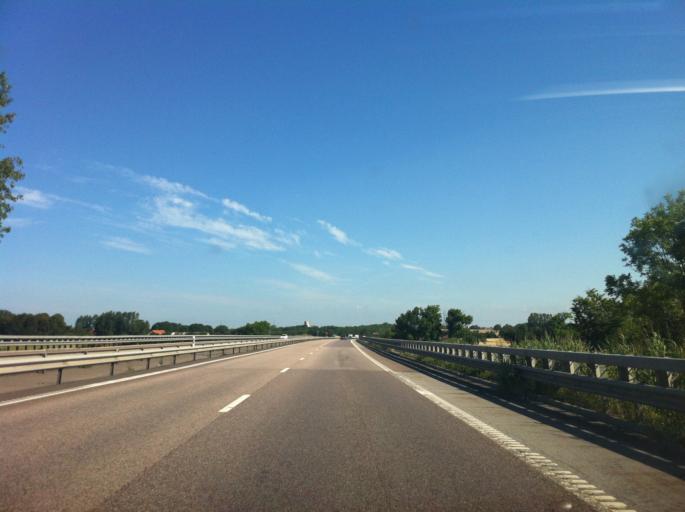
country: SE
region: Skane
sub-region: Helsingborg
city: Gantofta
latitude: 55.9843
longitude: 12.7825
